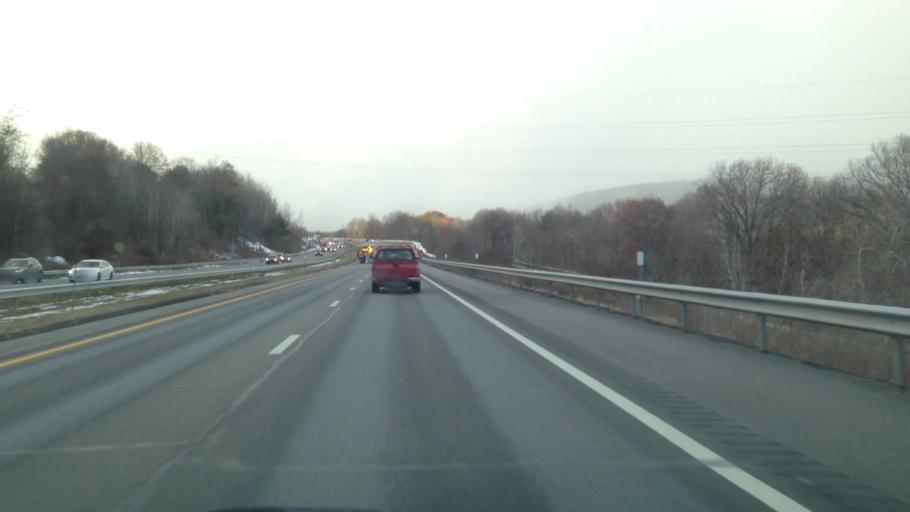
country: US
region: New York
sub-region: Schenectady County
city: Scotia
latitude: 42.8655
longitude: -74.0414
